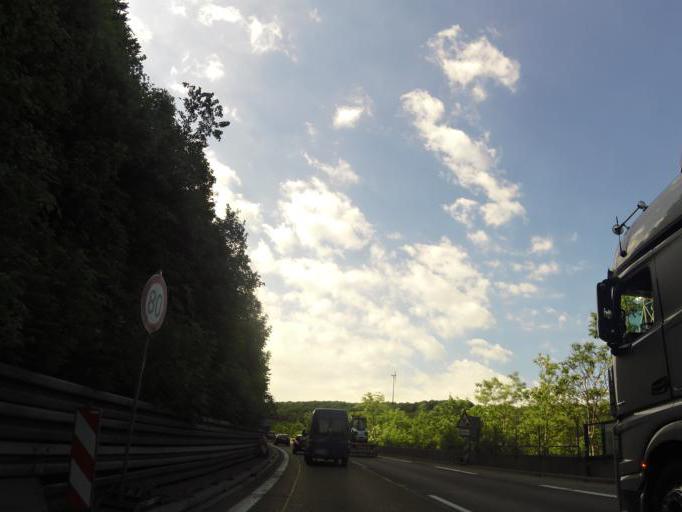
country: DE
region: Baden-Wuerttemberg
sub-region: Regierungsbezirk Stuttgart
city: Wiesensteig
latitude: 48.5592
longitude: 9.6302
